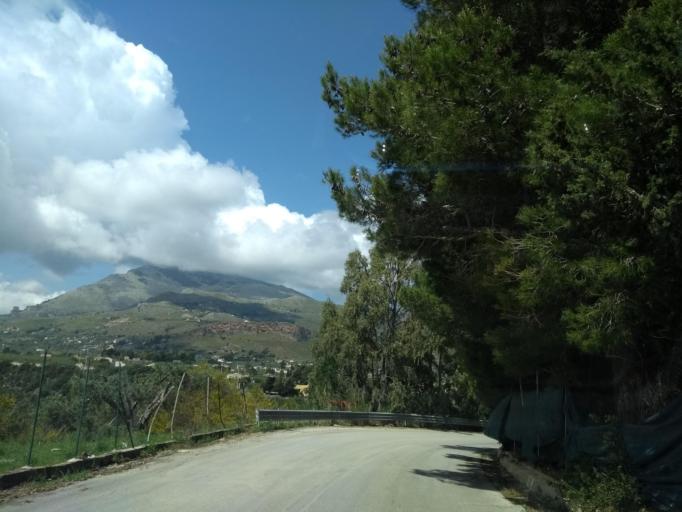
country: IT
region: Sicily
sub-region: Trapani
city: Castellammare del Golfo
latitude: 38.0460
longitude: 12.8434
